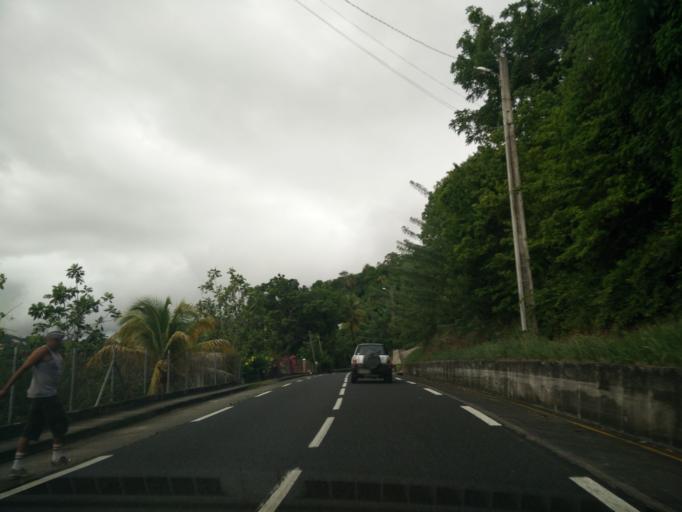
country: MQ
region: Martinique
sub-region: Martinique
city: Le Marin
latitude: 14.4834
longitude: -60.8613
